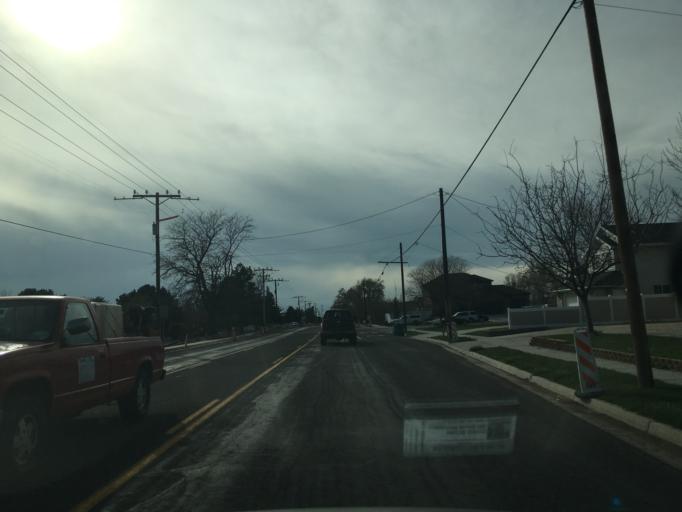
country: US
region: Utah
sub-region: Davis County
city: Layton
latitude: 41.0602
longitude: -111.9965
